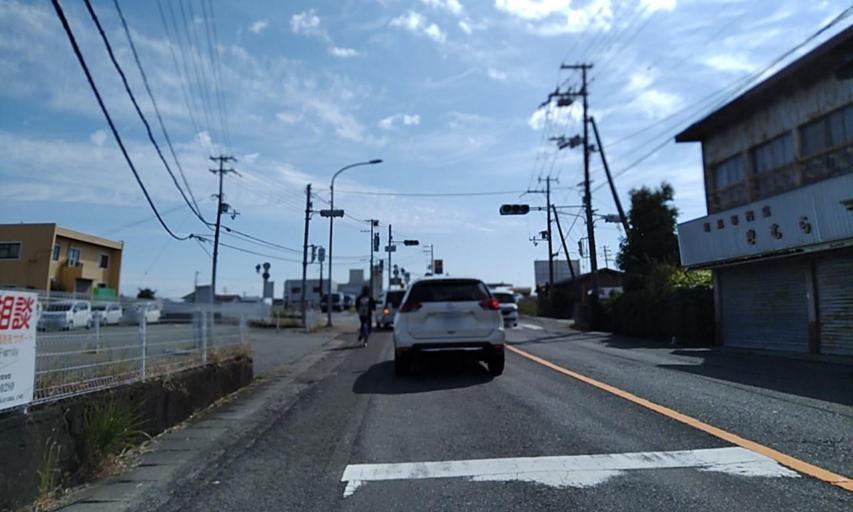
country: JP
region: Wakayama
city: Gobo
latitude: 33.9071
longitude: 135.1512
